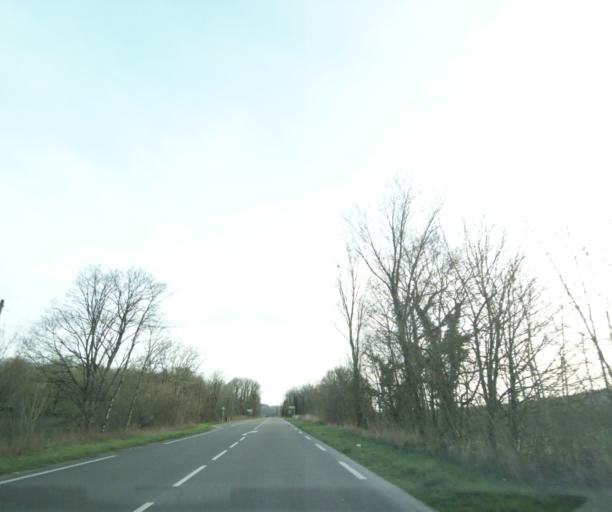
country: FR
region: Midi-Pyrenees
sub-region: Departement du Lot
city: Souillac
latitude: 44.9470
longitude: 1.4943
